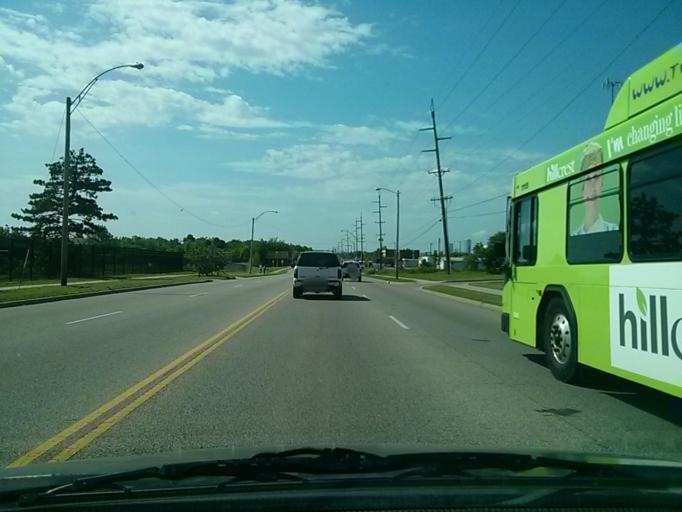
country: US
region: Oklahoma
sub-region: Tulsa County
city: Turley
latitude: 36.2085
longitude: -95.9756
